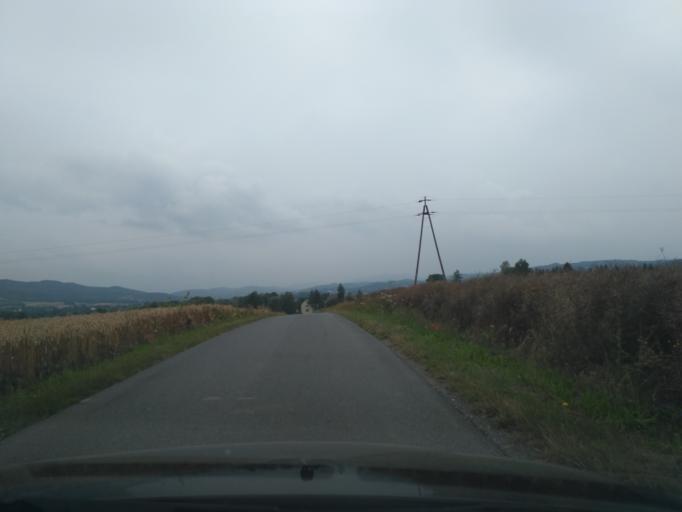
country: PL
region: Subcarpathian Voivodeship
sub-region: Powiat strzyzowski
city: Wysoka Strzyzowska
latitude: 49.8616
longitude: 21.7182
